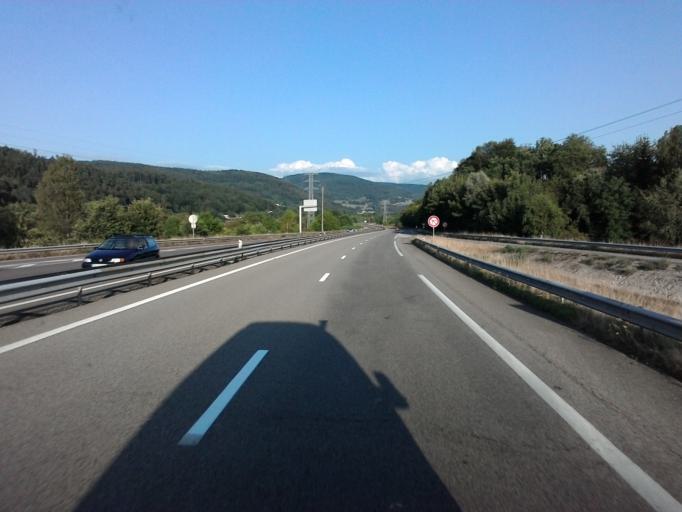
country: FR
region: Lorraine
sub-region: Departement des Vosges
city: Pouxeux
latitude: 48.1095
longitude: 6.5759
